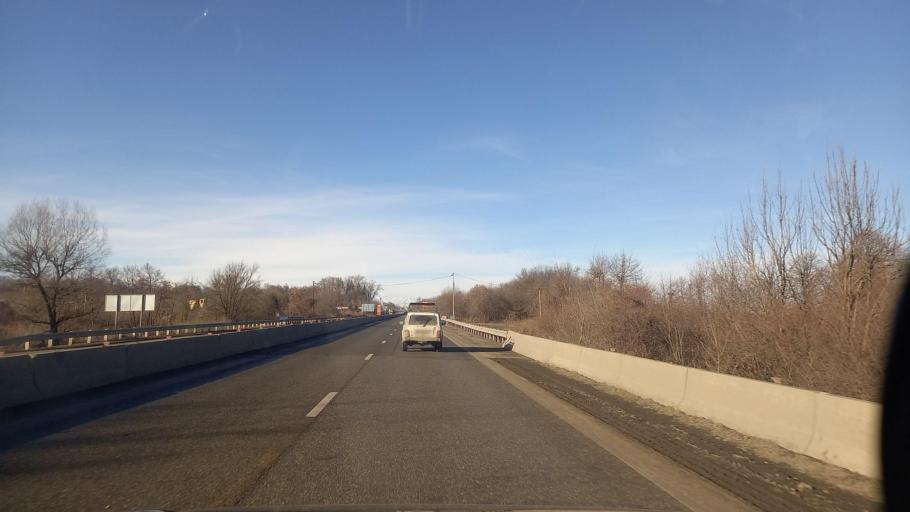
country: RU
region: North Ossetia
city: Gizel'
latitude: 43.0284
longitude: 44.5943
